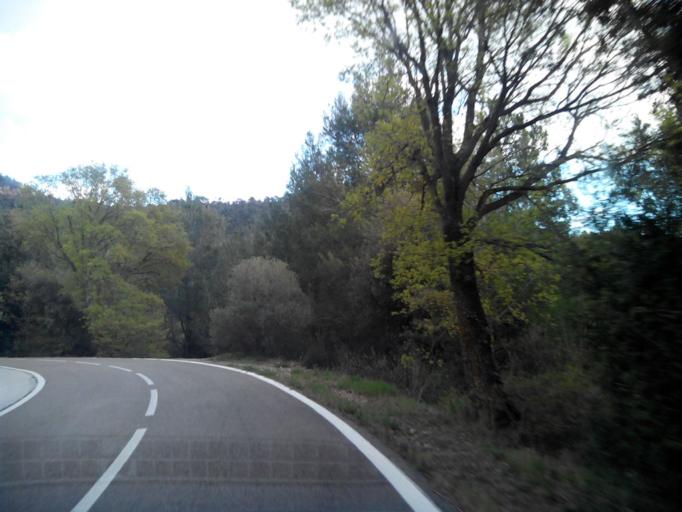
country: ES
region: Catalonia
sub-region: Provincia de Tarragona
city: Vilaplana
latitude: 41.2386
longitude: 1.0456
